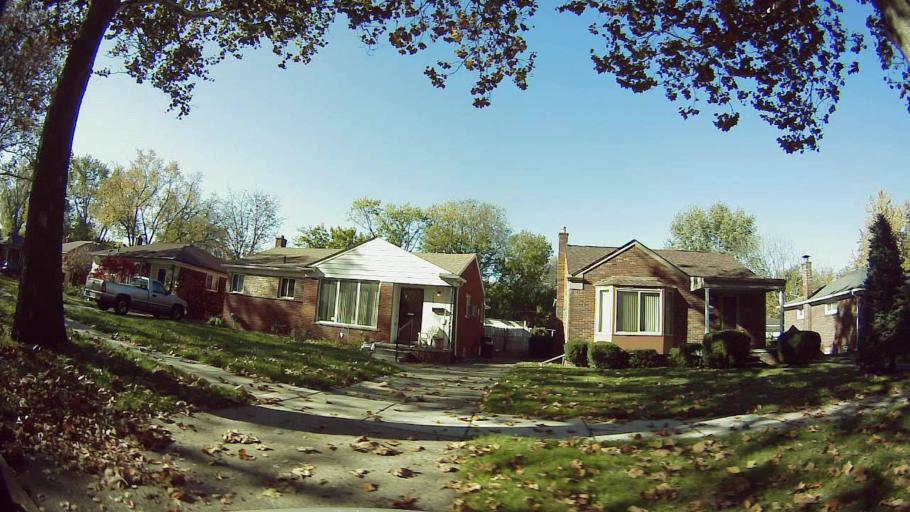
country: US
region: Michigan
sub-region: Oakland County
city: Huntington Woods
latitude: 42.4679
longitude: -83.1626
